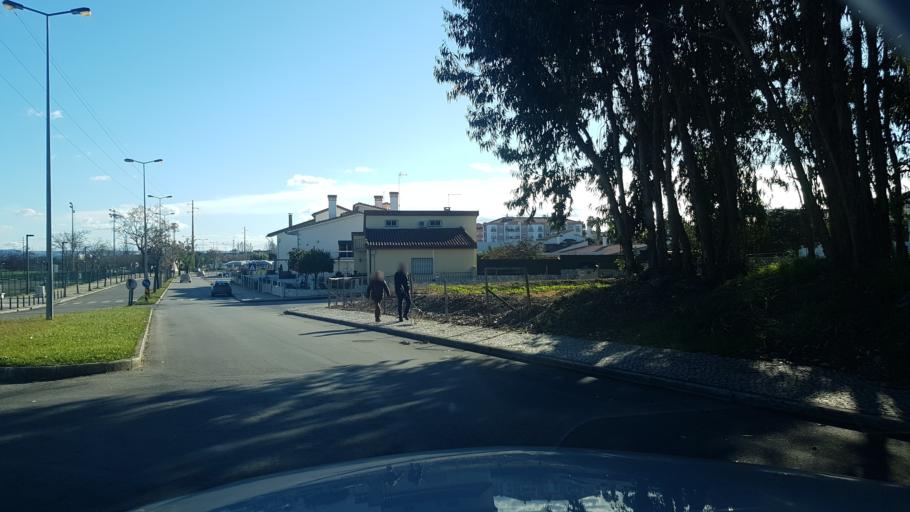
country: PT
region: Santarem
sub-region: Entroncamento
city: Entroncamento
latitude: 39.4762
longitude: -8.4682
